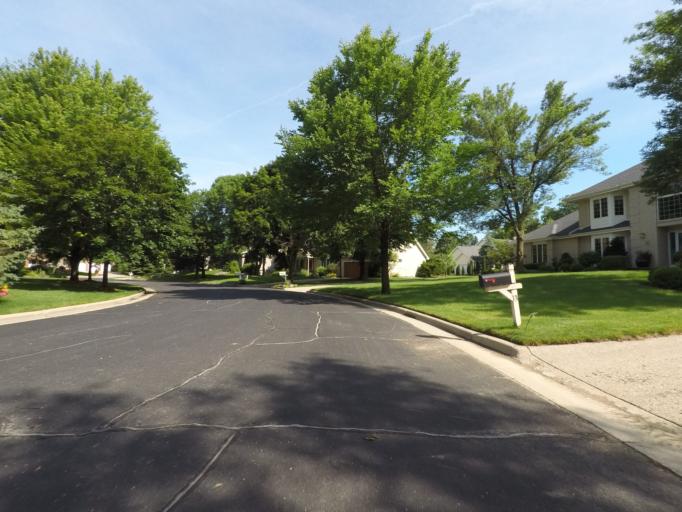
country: US
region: Wisconsin
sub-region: Dane County
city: Middleton
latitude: 43.0807
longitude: -89.4929
